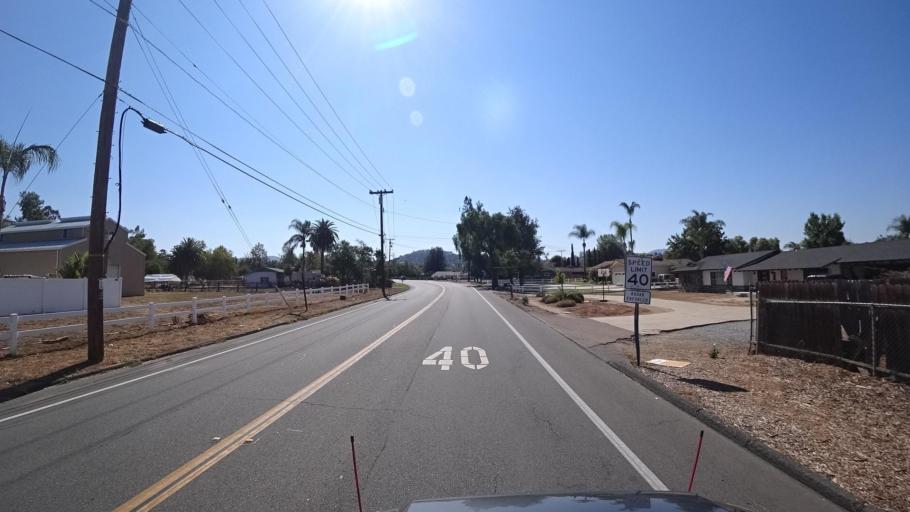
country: US
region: California
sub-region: San Diego County
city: Granite Hills
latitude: 32.7923
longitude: -116.9206
